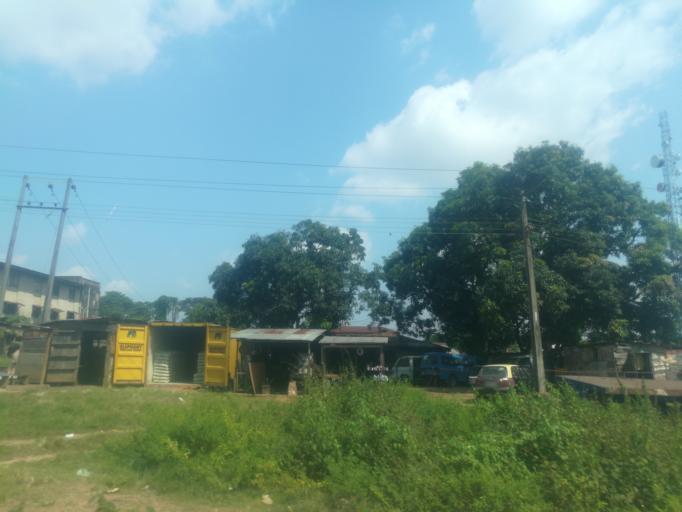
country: NG
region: Oyo
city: Moniya
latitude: 7.5105
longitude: 3.9126
